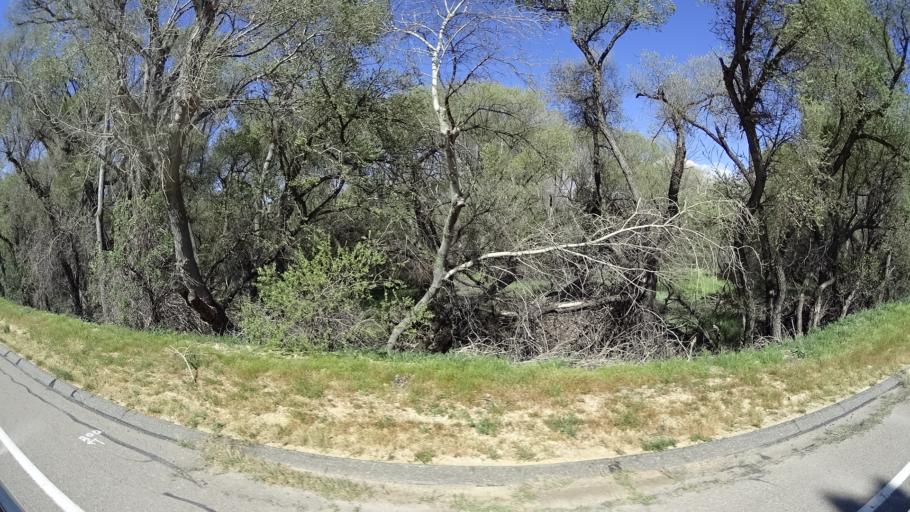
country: US
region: California
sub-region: San Diego County
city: Julian
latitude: 33.2451
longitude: -116.6698
